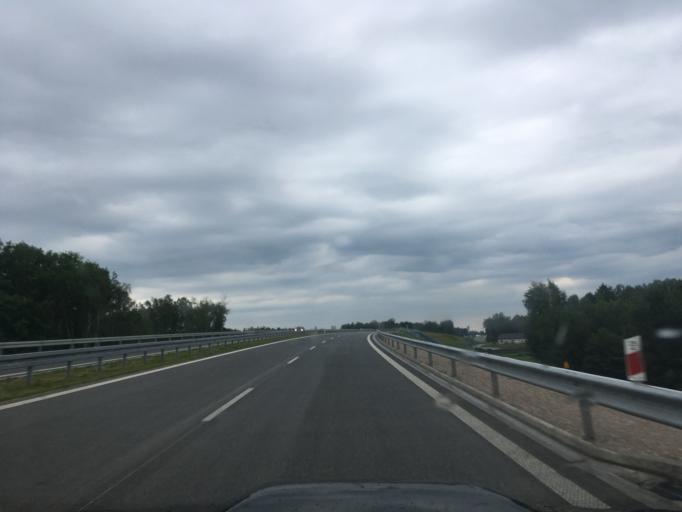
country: PL
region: Masovian Voivodeship
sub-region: Powiat piaseczynski
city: Gora Kalwaria
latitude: 51.9840
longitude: 21.1741
